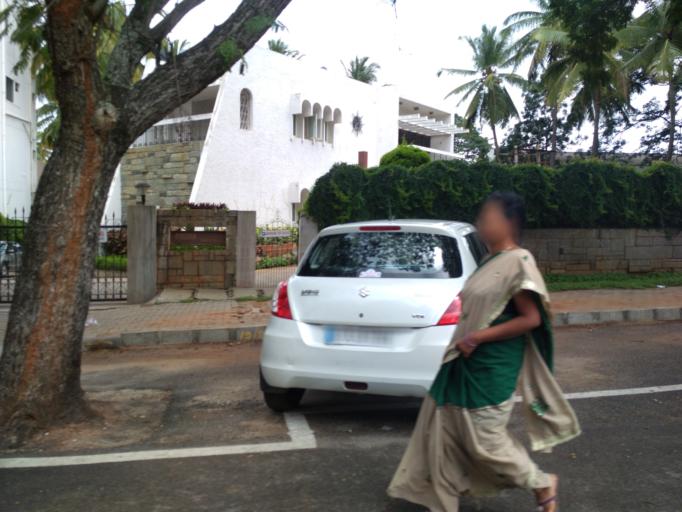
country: IN
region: Karnataka
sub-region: Mysore
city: Mysore
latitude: 12.3255
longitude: 76.6326
